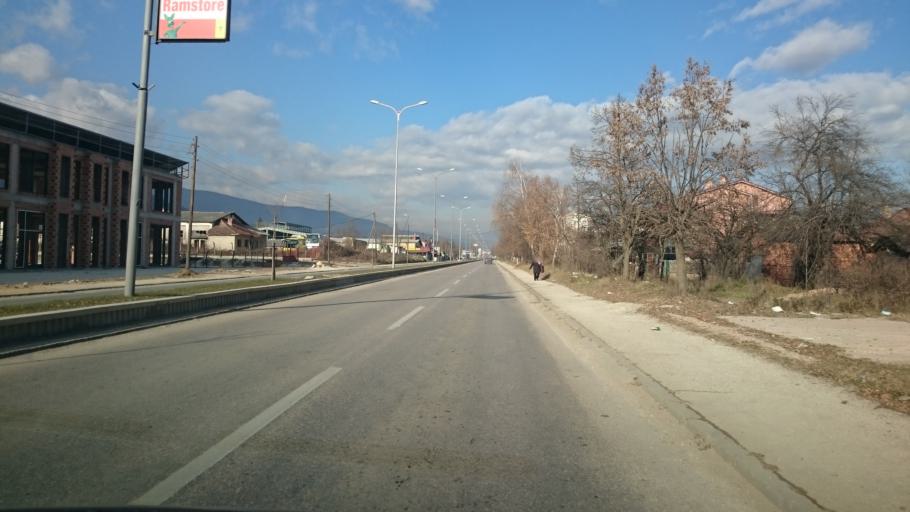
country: MK
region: Kicevo
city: Kicevo
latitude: 41.5082
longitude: 20.9525
